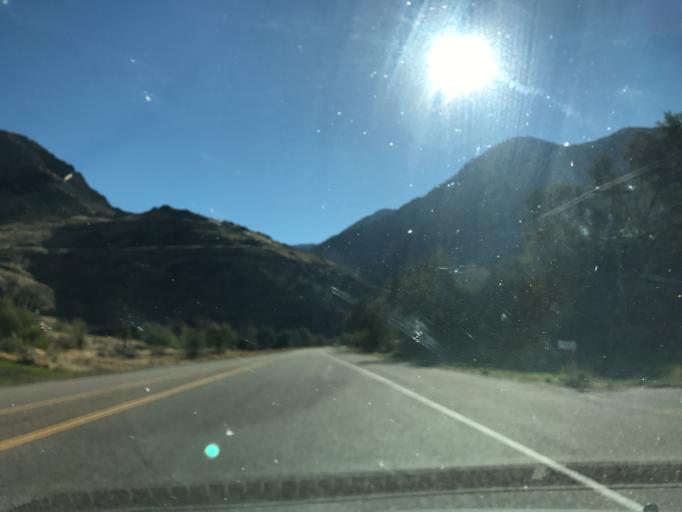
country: US
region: Utah
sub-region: Weber County
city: Ogden
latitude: 41.2394
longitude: -111.9346
